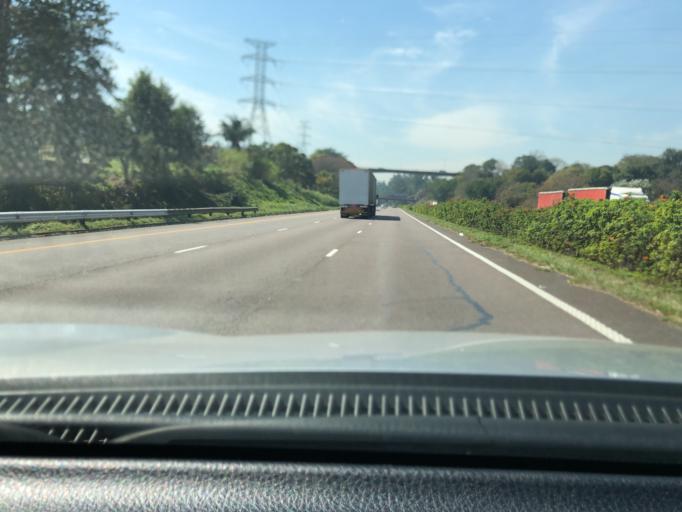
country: ZA
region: KwaZulu-Natal
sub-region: eThekwini Metropolitan Municipality
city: Berea
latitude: -29.8382
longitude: 30.8715
